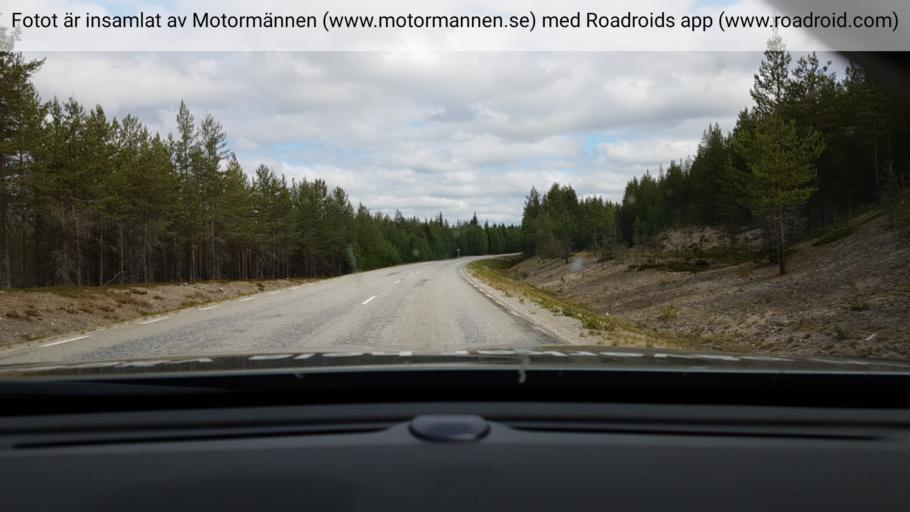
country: SE
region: Vaesterbotten
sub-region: Mala Kommun
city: Mala
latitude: 64.9259
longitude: 18.6184
